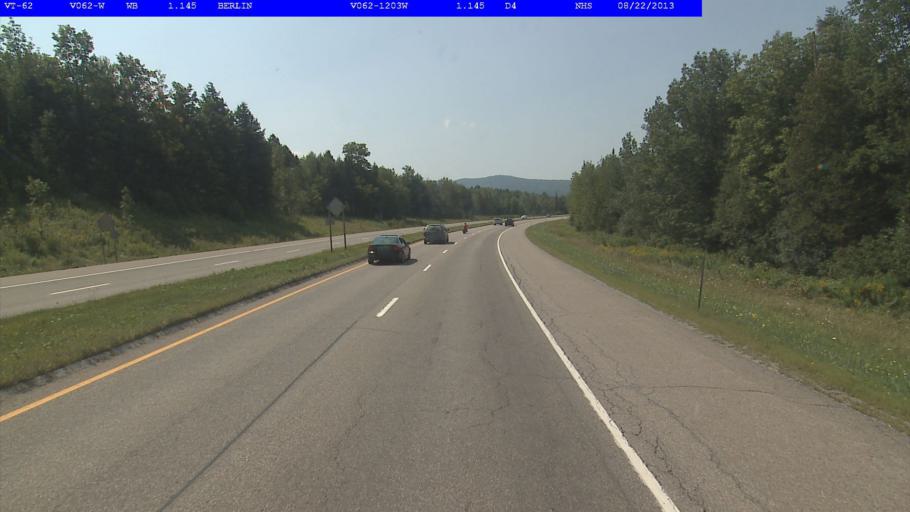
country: US
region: Vermont
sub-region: Washington County
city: Montpelier
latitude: 44.2152
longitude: -72.5625
